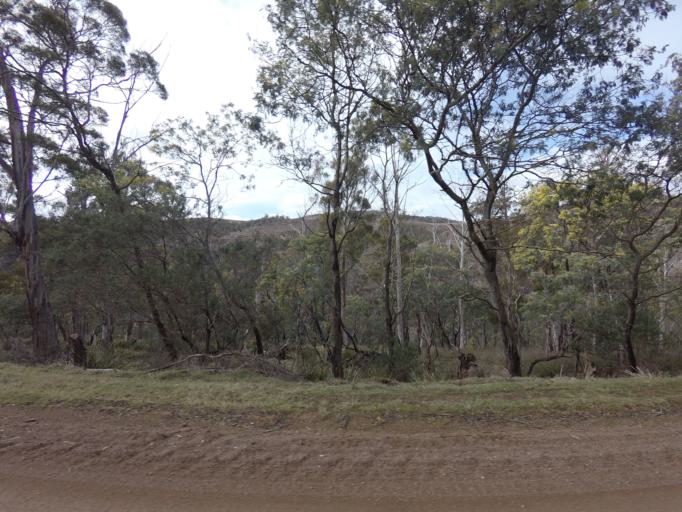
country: AU
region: Tasmania
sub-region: Derwent Valley
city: New Norfolk
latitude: -42.7387
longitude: 146.8702
